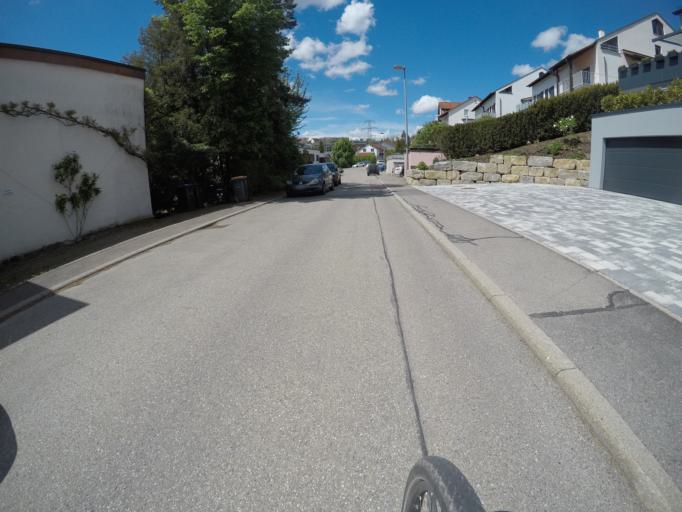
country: DE
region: Baden-Wuerttemberg
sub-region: Regierungsbezirk Stuttgart
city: Holzgerlingen
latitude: 48.6437
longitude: 9.0218
